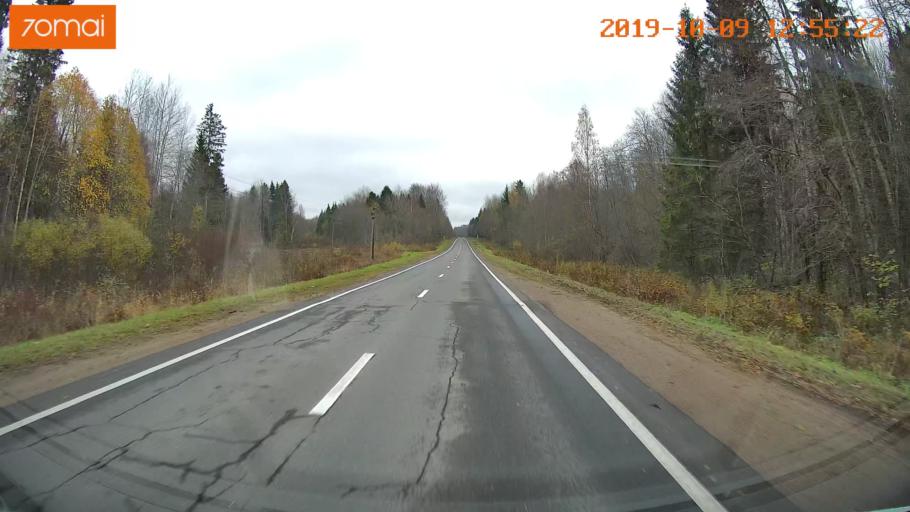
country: RU
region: Jaroslavl
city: Prechistoye
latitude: 58.4002
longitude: 40.3920
